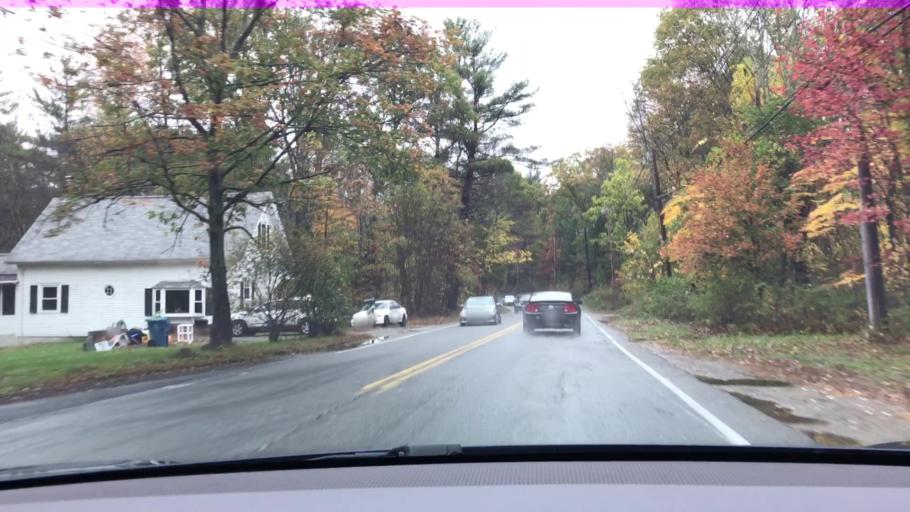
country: US
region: Massachusetts
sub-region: Middlesex County
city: Billerica
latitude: 42.5323
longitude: -71.2848
